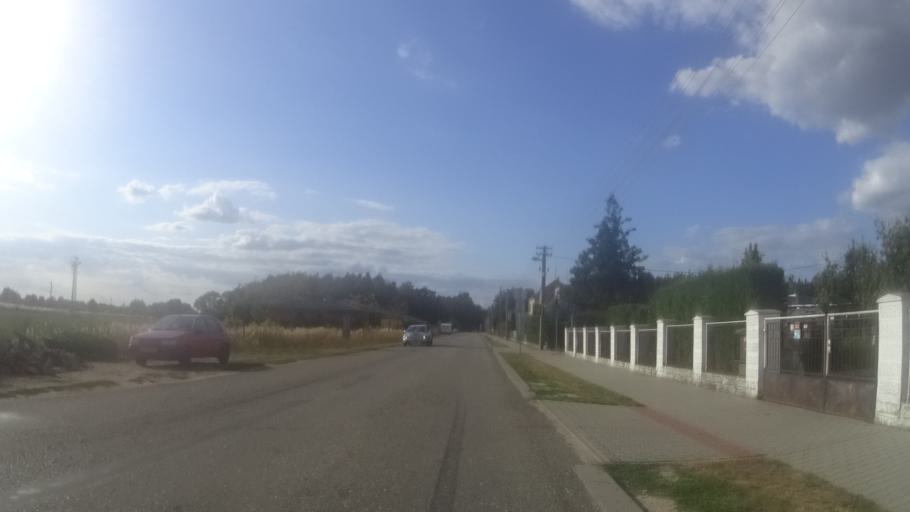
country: CZ
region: Kralovehradecky
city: Trebechovice pod Orebem
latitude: 50.1914
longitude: 16.0050
